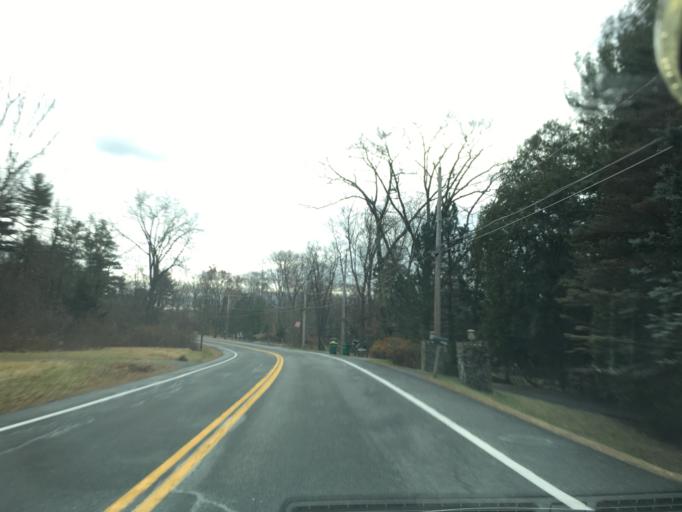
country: US
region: New York
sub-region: Rensselaer County
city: Averill Park
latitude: 42.6234
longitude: -73.5278
